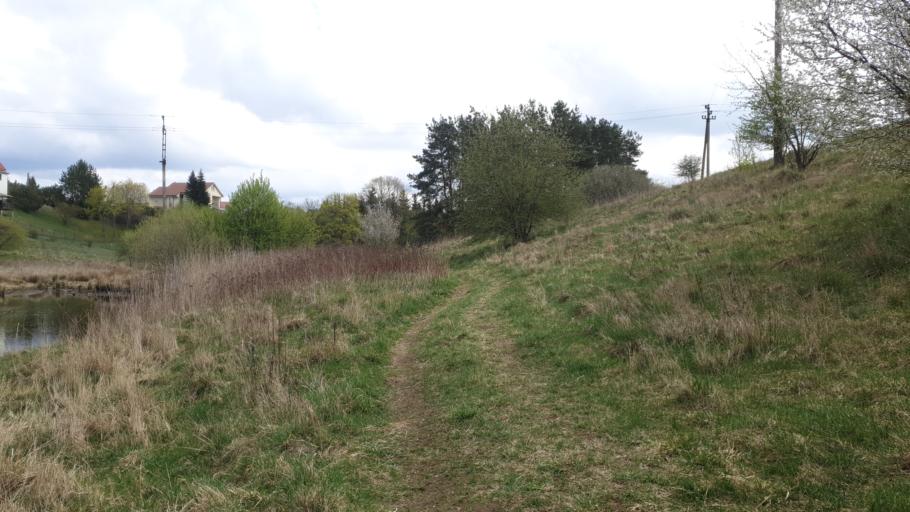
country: LT
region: Vilnius County
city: Pilaite
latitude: 54.7264
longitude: 25.1906
